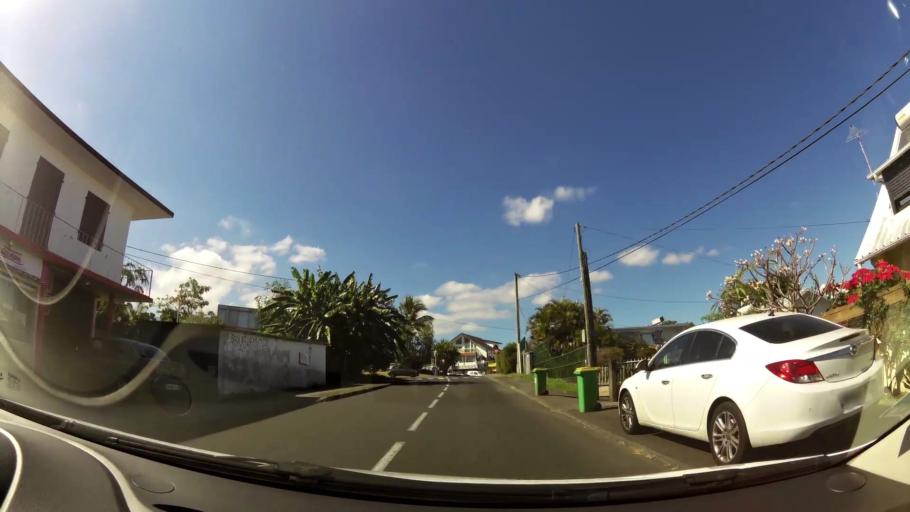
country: RE
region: Reunion
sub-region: Reunion
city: Le Tampon
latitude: -21.2880
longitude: 55.5111
